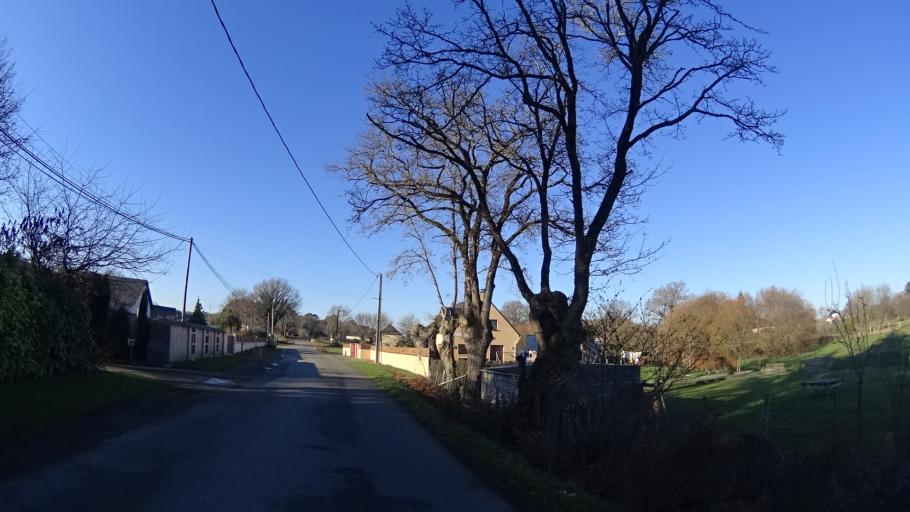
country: FR
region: Brittany
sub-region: Departement du Morbihan
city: Allaire
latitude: 47.6406
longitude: -2.1724
